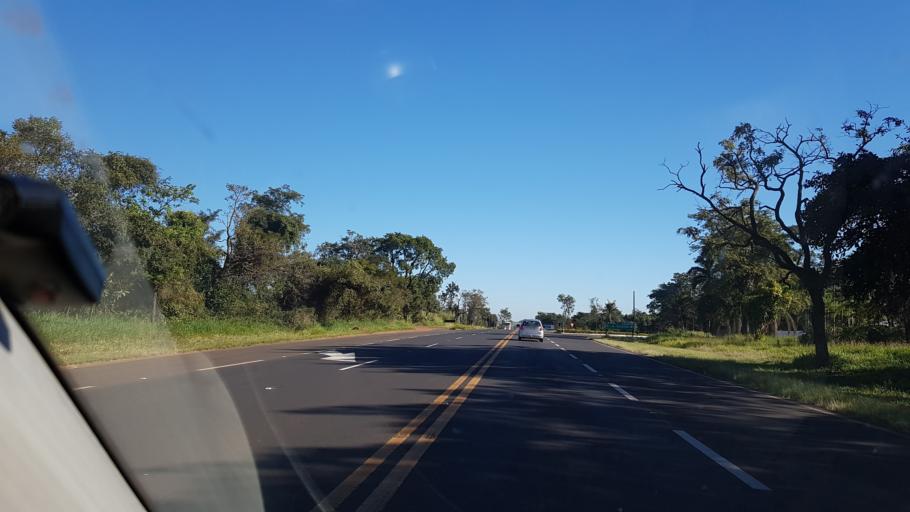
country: BR
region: Sao Paulo
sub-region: Assis
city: Assis
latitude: -22.6194
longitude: -50.4554
